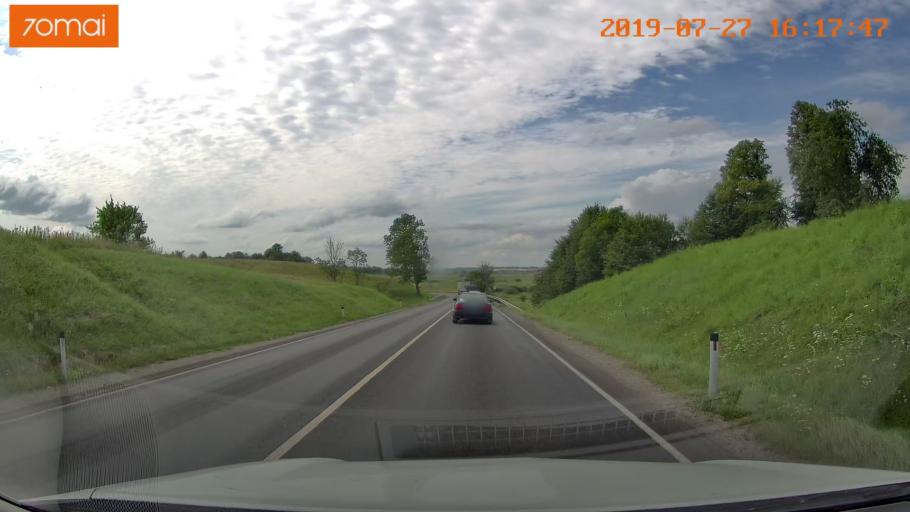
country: RU
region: Kaliningrad
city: Chernyakhovsk
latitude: 54.6241
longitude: 21.5443
